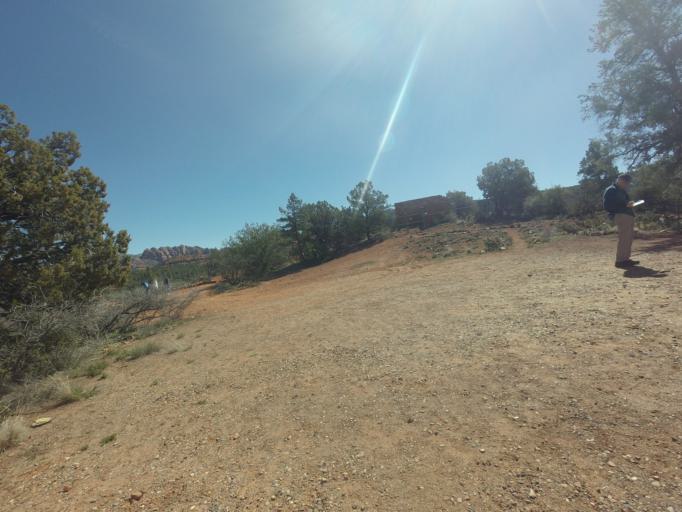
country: US
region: Arizona
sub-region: Yavapai County
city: West Sedona
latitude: 34.8082
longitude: -111.8252
